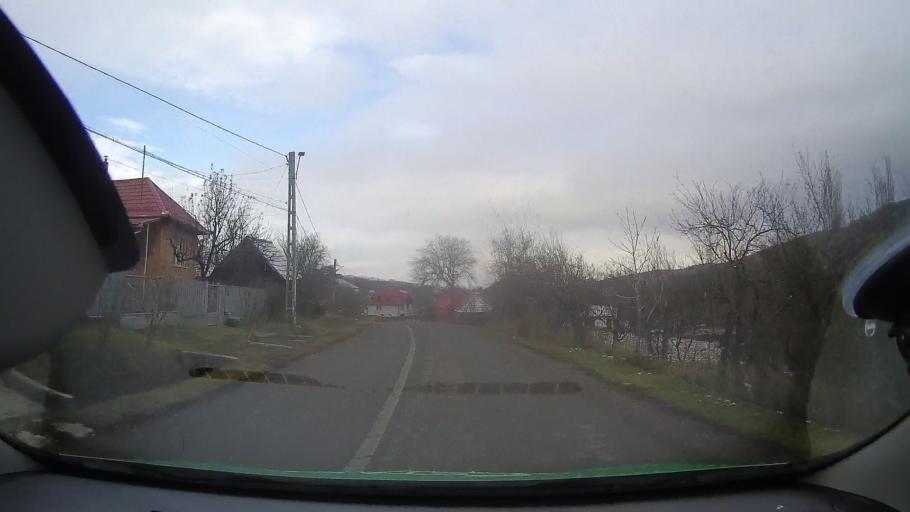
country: RO
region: Alba
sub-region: Comuna Farau
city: Farau
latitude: 46.3919
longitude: 24.0360
